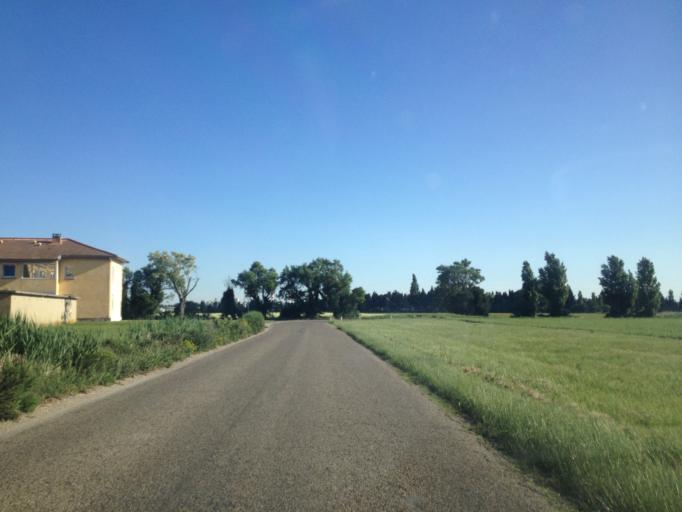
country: FR
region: Provence-Alpes-Cote d'Azur
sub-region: Departement du Vaucluse
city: Orange
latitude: 44.1403
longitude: 4.8441
